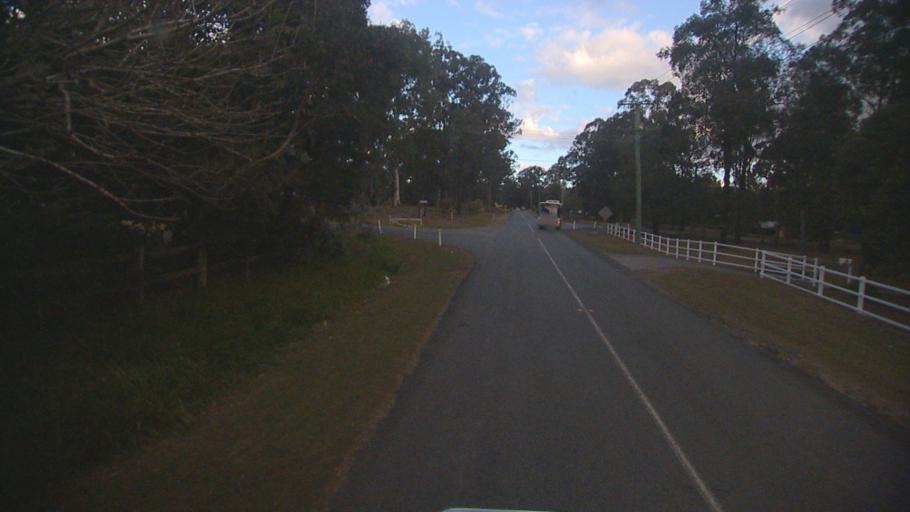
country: AU
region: Queensland
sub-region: Logan
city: Chambers Flat
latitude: -27.7866
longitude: 153.1358
